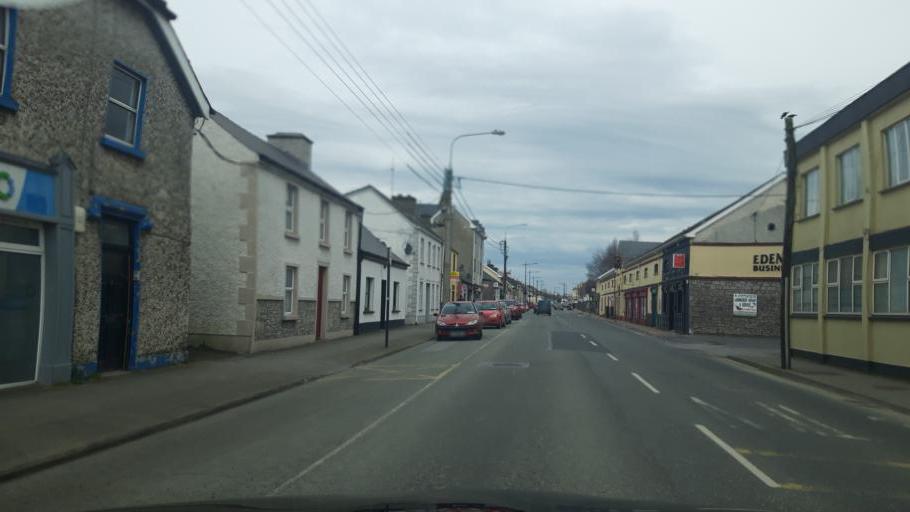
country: IE
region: Leinster
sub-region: Uibh Fhaili
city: Edenderry
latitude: 53.3396
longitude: -7.0578
